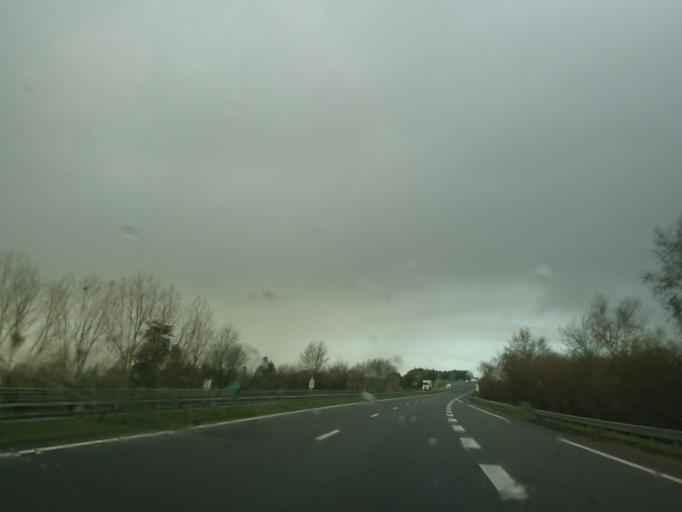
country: FR
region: Brittany
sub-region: Departement d'Ille-et-Vilaine
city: Quedillac
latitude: 48.2230
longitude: -2.1122
